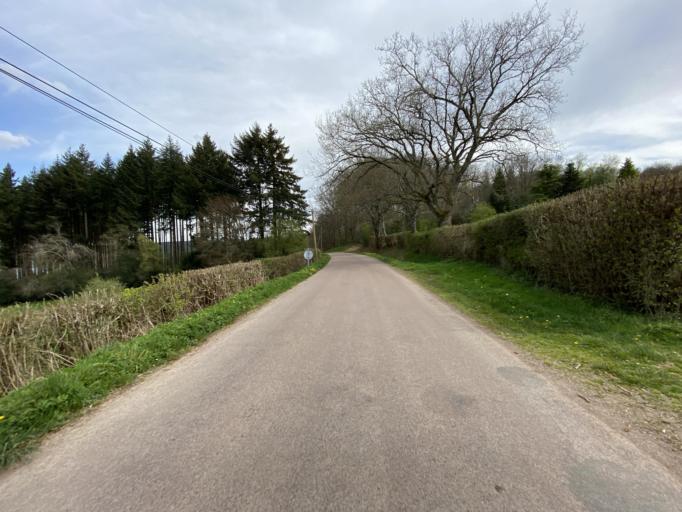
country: FR
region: Bourgogne
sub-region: Departement de la Cote-d'Or
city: Saulieu
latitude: 47.3214
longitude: 4.0812
